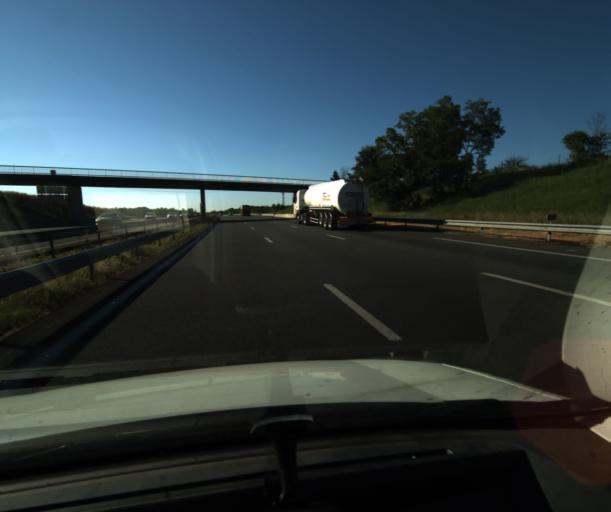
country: FR
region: Midi-Pyrenees
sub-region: Departement de la Haute-Garonne
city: Castelnau-d'Estretefonds
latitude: 43.7987
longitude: 1.3717
